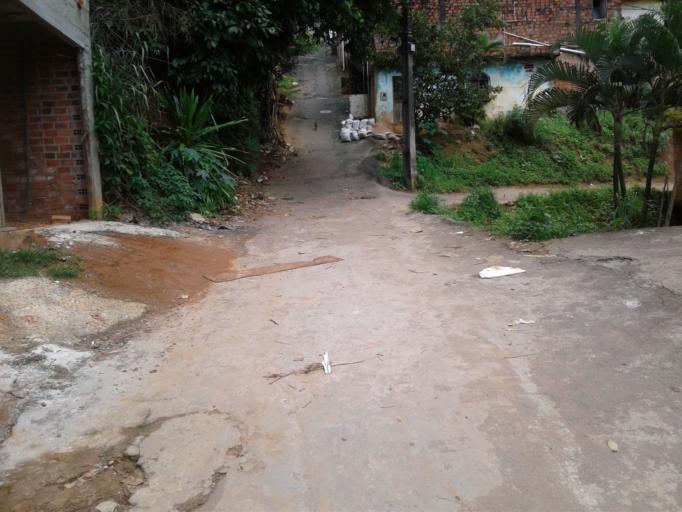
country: BR
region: Bahia
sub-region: Salvador
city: Salvador
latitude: -12.9113
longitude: -38.4747
